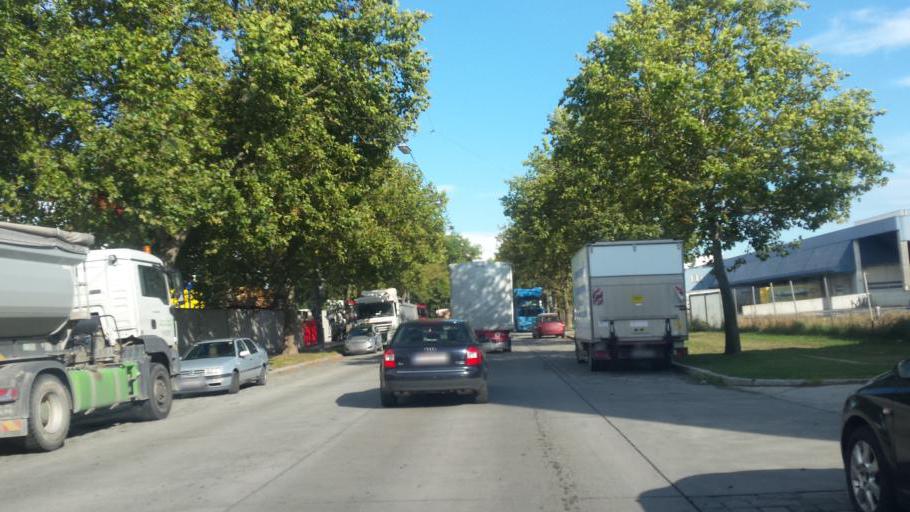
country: AT
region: Lower Austria
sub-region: Politischer Bezirk Wien-Umgebung
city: Schwechat
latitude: 48.1789
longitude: 16.4434
